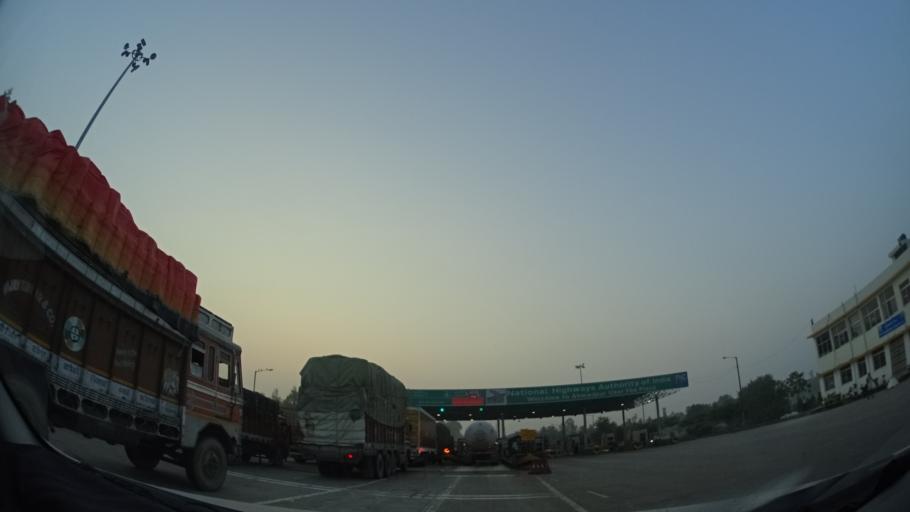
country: IN
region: Uttar Pradesh
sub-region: Bara Banki
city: Zaidpur
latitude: 26.8586
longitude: 81.4220
